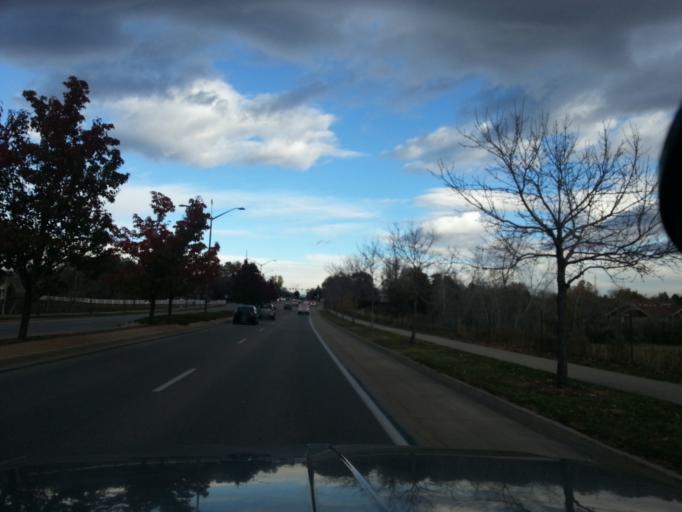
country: US
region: Colorado
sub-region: Larimer County
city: Fort Collins
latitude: 40.5503
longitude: -105.1150
